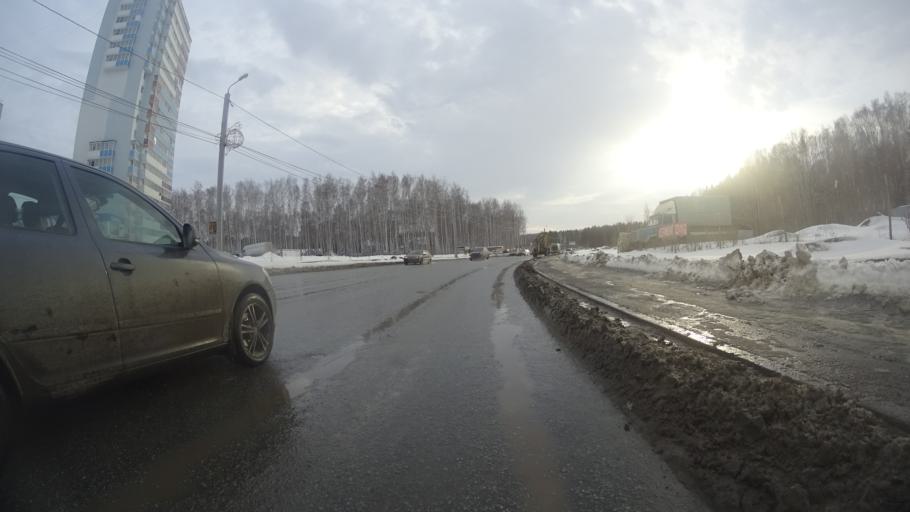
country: RU
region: Chelyabinsk
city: Roshchino
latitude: 55.2023
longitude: 61.2839
